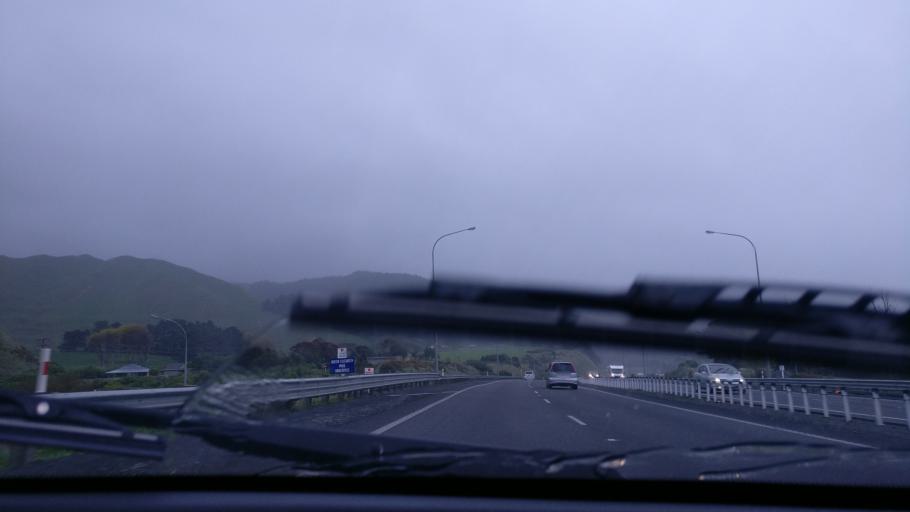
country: NZ
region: Wellington
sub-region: Kapiti Coast District
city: Paraparaumu
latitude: -40.9706
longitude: 174.9833
